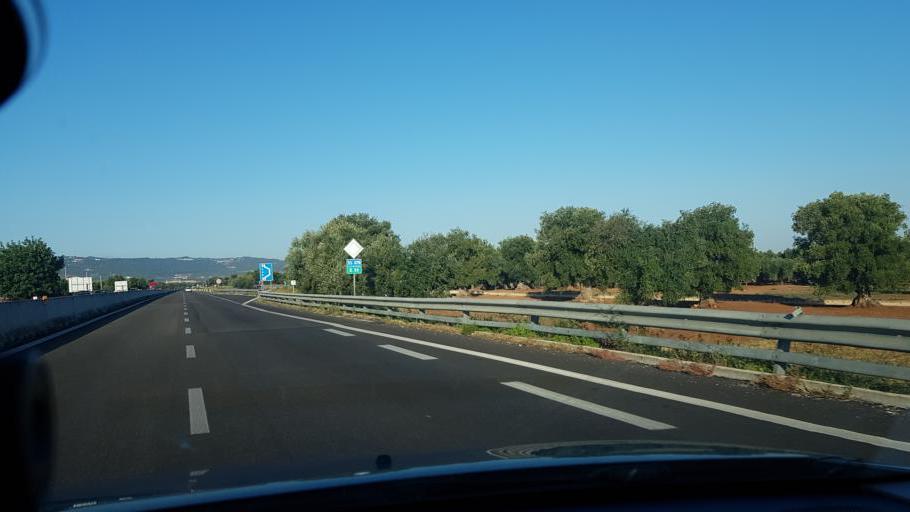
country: IT
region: Apulia
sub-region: Provincia di Brindisi
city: Pezze di Greco
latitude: 40.8339
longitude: 17.4044
